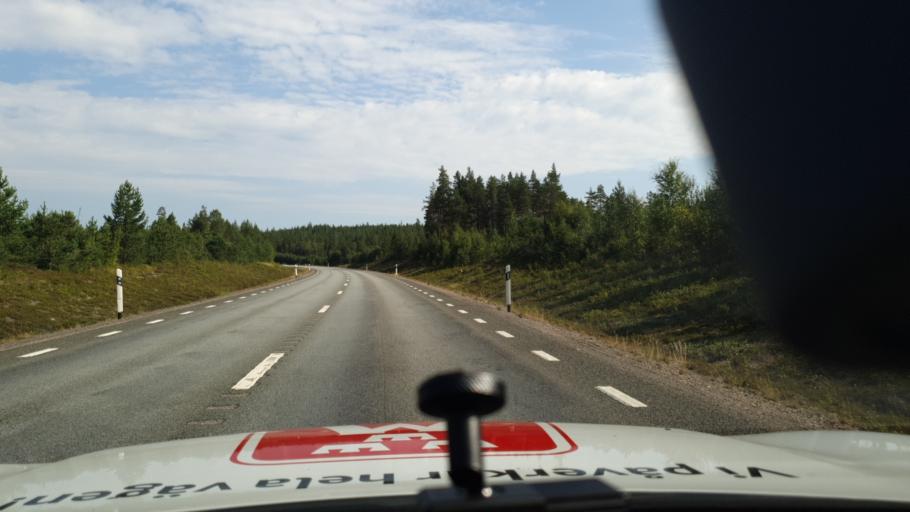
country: SE
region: Vaermland
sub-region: Hagfors Kommun
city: Ekshaerad
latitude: 60.5009
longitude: 13.4238
